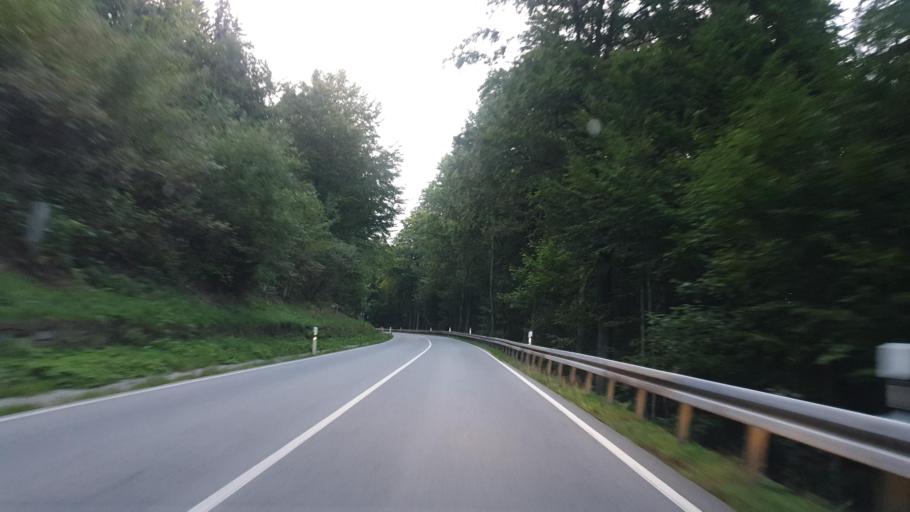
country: DE
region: Saxony
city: Sosa
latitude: 50.4734
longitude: 12.6282
